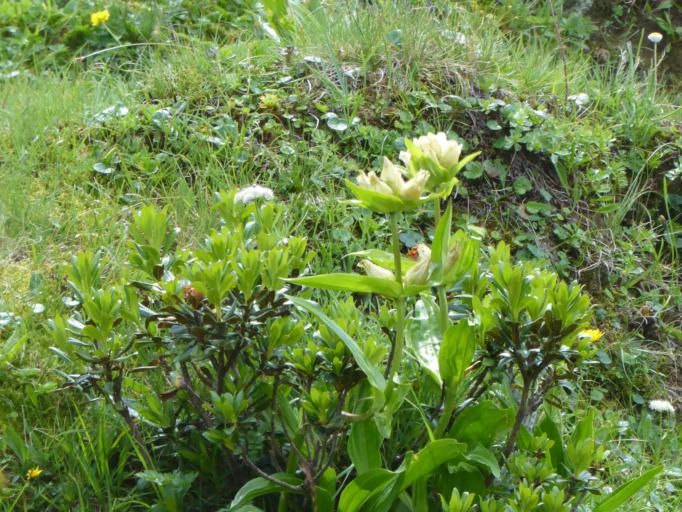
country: IT
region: Trentino-Alto Adige
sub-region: Bolzano
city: Predoi
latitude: 46.9823
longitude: 12.1256
